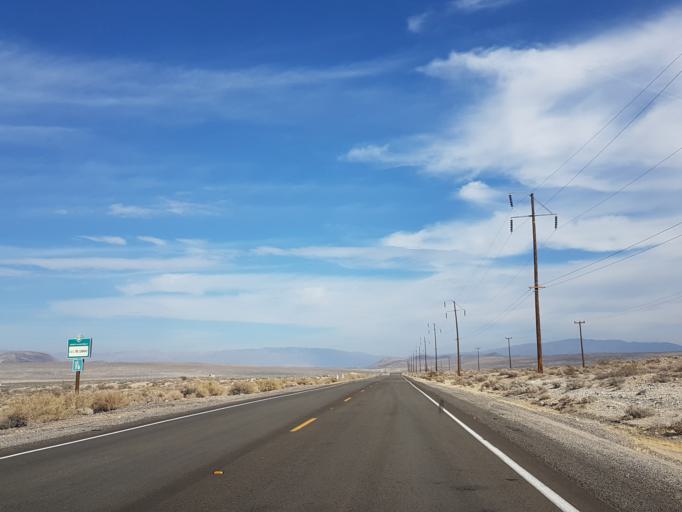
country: US
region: California
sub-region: Kern County
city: Ridgecrest
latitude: 35.6460
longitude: -117.5198
